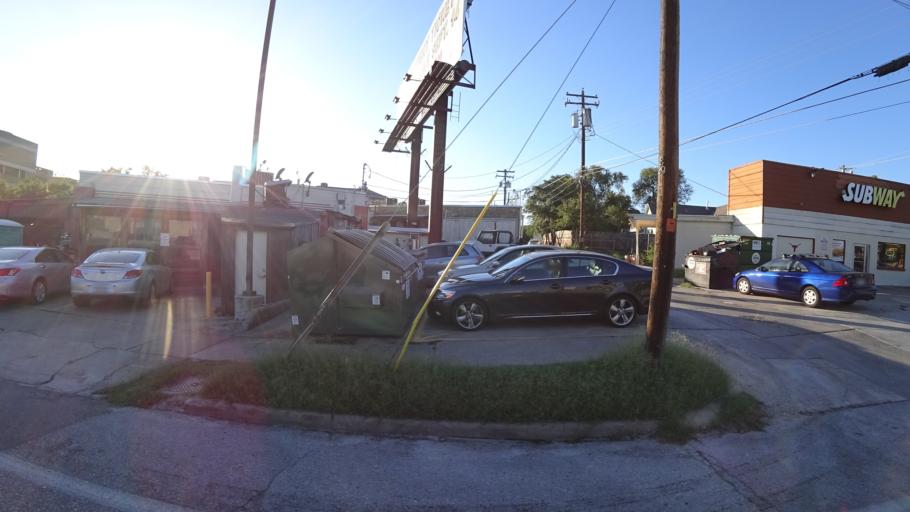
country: US
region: Texas
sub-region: Travis County
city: Austin
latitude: 30.2914
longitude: -97.7345
